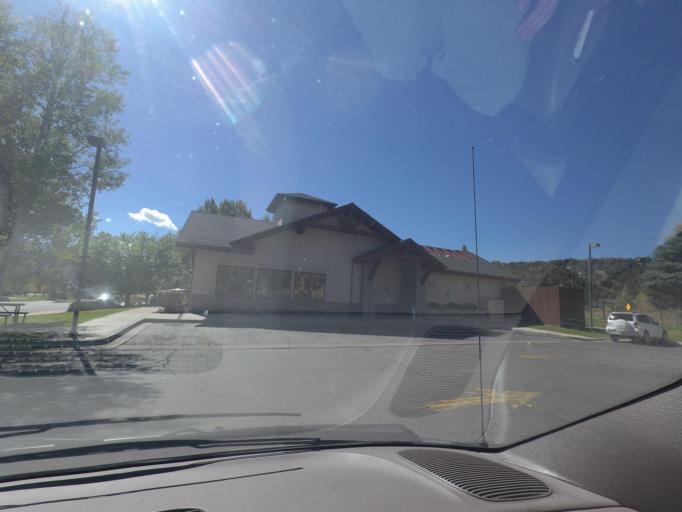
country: US
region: Colorado
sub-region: Eagle County
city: Eagle
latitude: 39.6598
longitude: -106.8261
